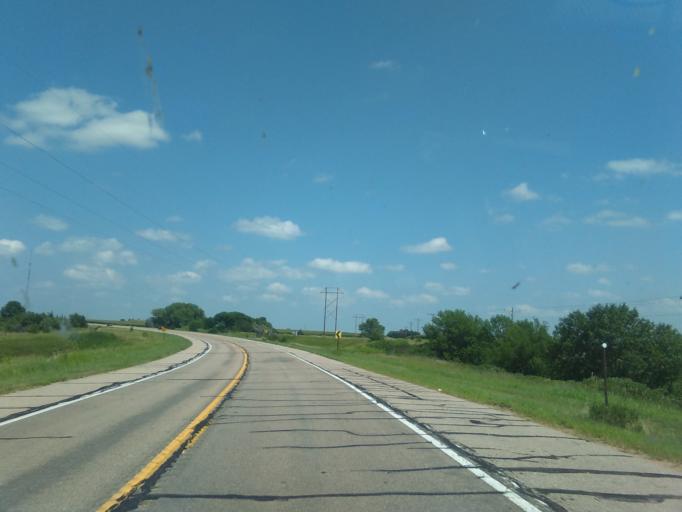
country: US
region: Nebraska
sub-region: Gosper County
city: Elwood
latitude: 40.6844
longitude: -99.8020
